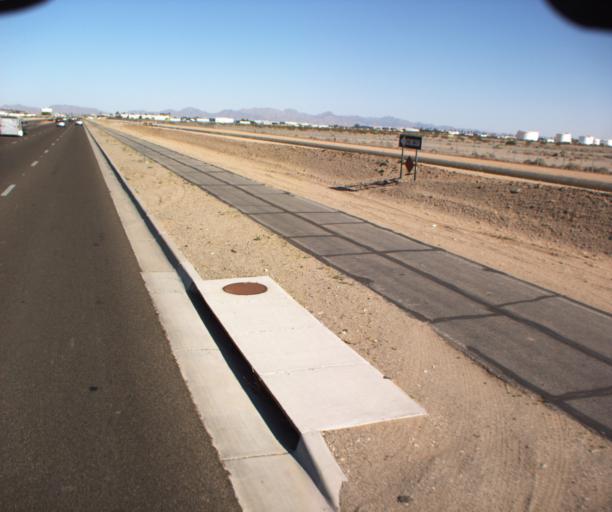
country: US
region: Arizona
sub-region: Yuma County
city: Yuma
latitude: 32.6694
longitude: -114.5918
